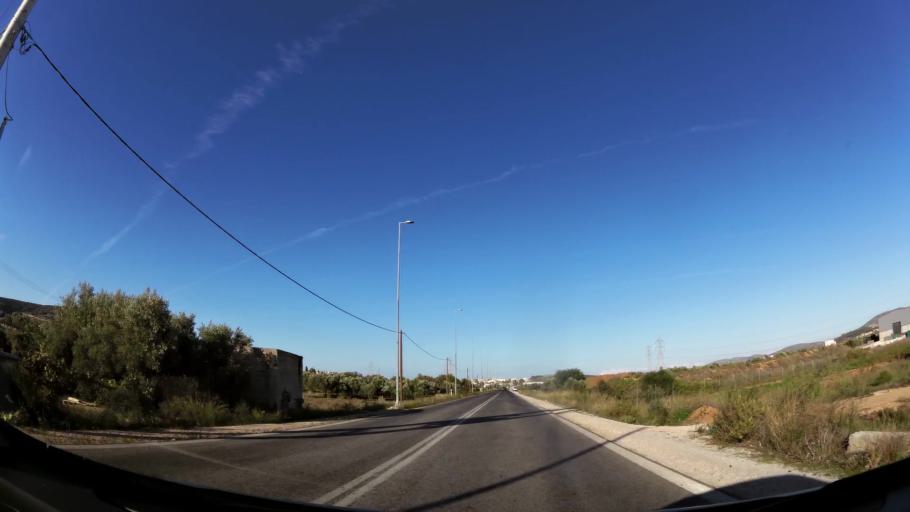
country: GR
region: Attica
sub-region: Nomarchia Anatolikis Attikis
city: Kalyvia Thorikou
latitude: 37.8601
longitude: 23.9221
